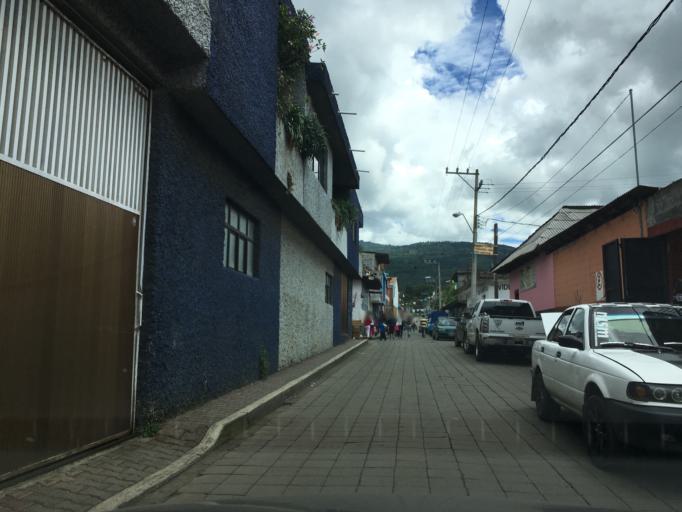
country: MX
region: Michoacan
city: Nahuatzen
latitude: 19.6535
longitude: -101.9165
